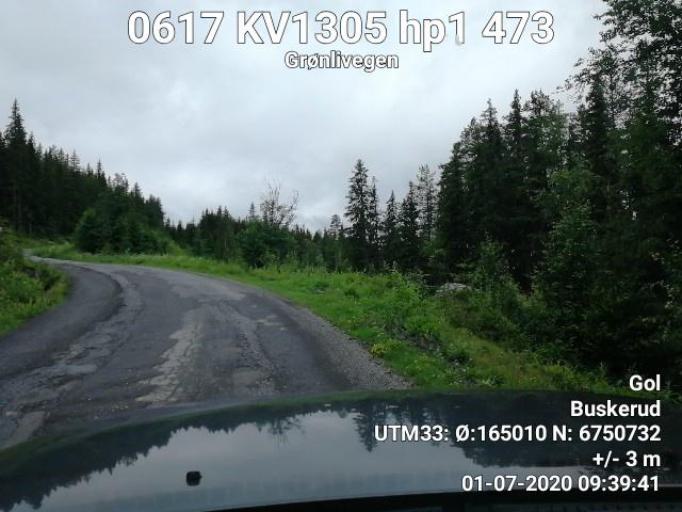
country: NO
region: Buskerud
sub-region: Gol
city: Gol
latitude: 60.7507
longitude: 8.8482
